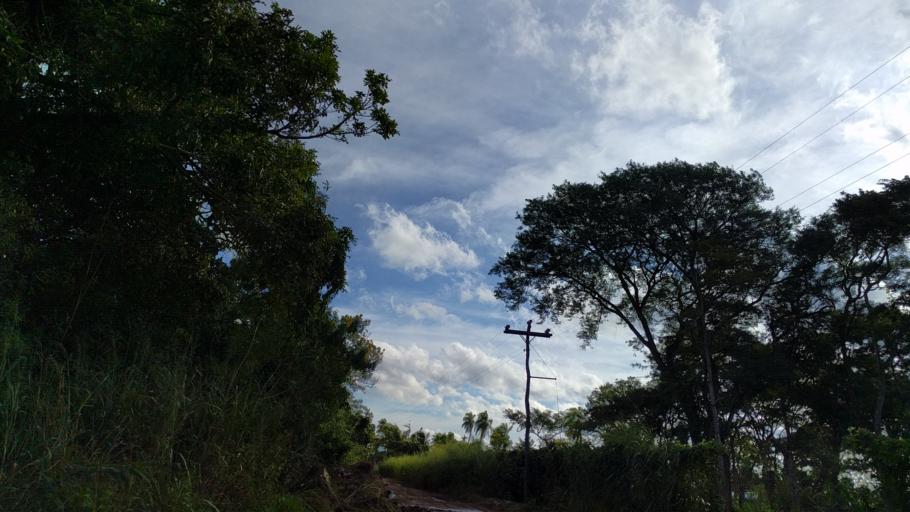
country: BO
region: Santa Cruz
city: Santa Cruz de la Sierra
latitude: -17.8530
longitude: -63.2625
